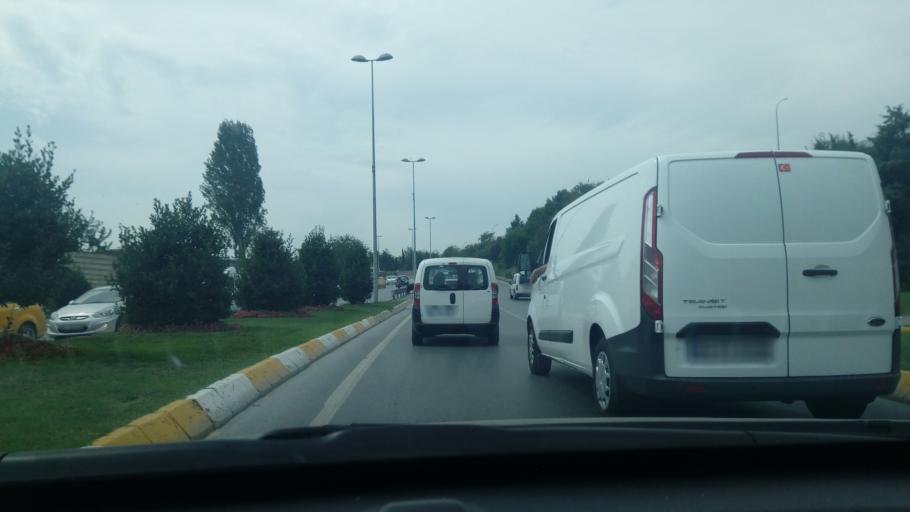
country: TR
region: Istanbul
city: Istanbul
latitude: 41.0405
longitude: 28.9410
